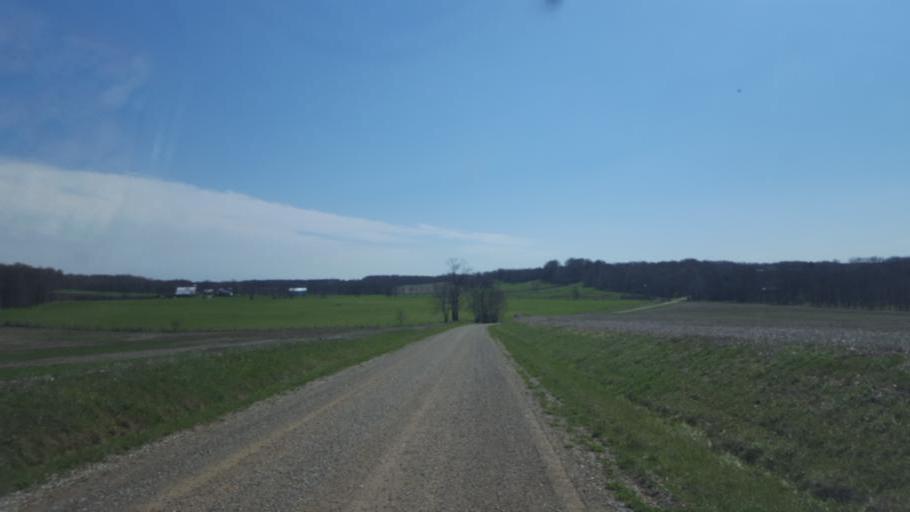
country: US
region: Ohio
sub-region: Knox County
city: Gambier
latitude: 40.3469
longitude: -82.3701
